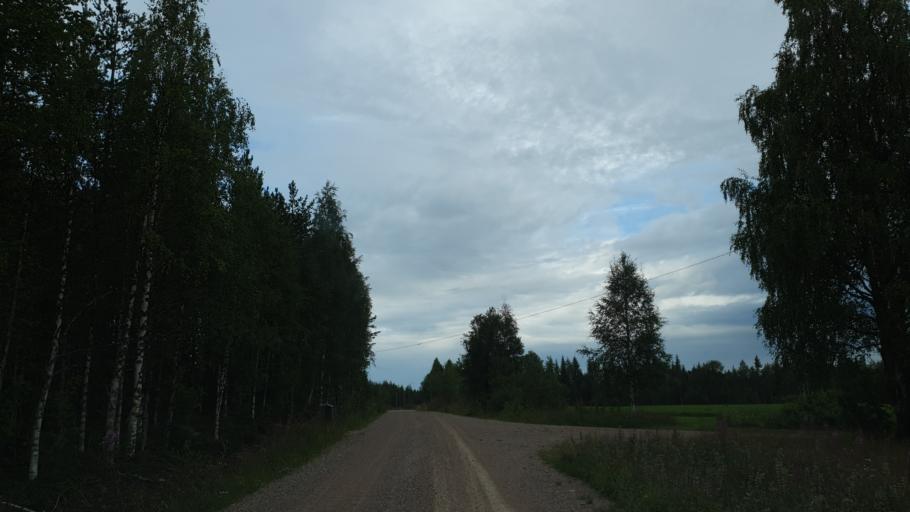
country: FI
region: Kainuu
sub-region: Kehys-Kainuu
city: Suomussalmi
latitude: 64.4450
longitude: 28.9670
